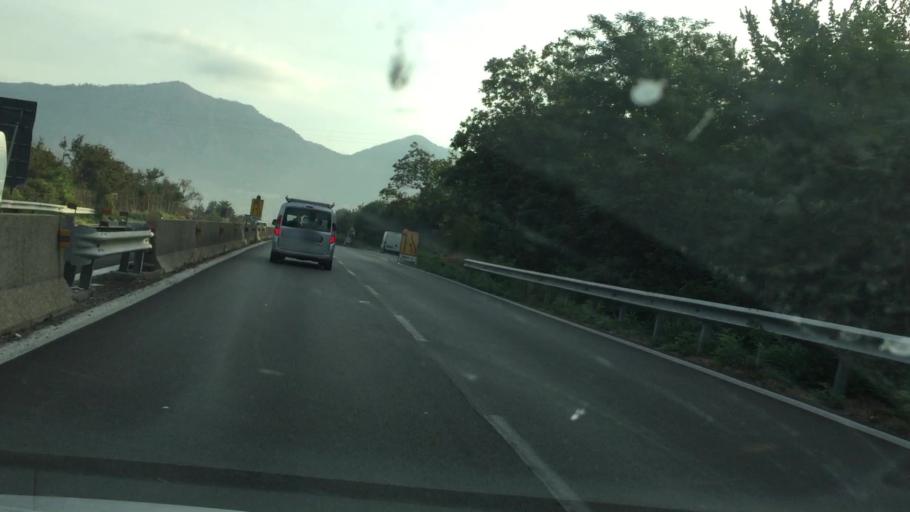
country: IT
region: Campania
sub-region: Provincia di Avellino
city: Torchiati
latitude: 40.8234
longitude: 14.8084
